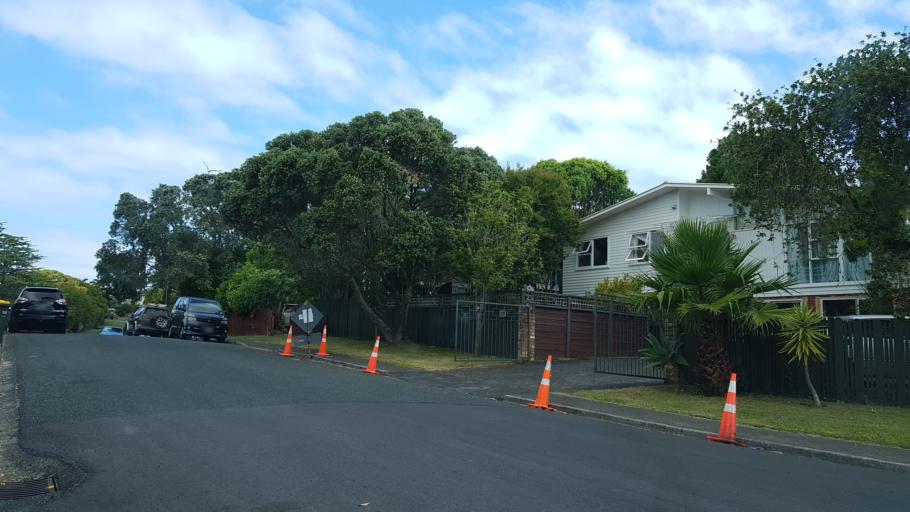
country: NZ
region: Auckland
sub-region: Auckland
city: North Shore
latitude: -36.7766
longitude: 174.7282
